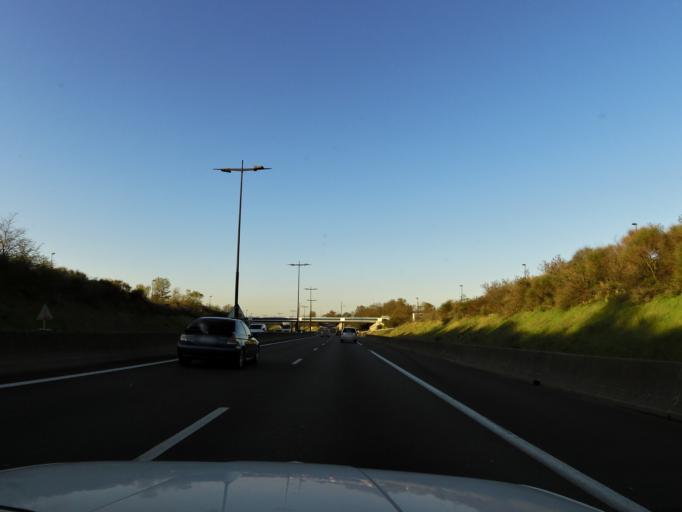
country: FR
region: Rhone-Alpes
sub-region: Departement du Rhone
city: Decines-Charpieu
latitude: 45.7711
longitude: 4.9848
